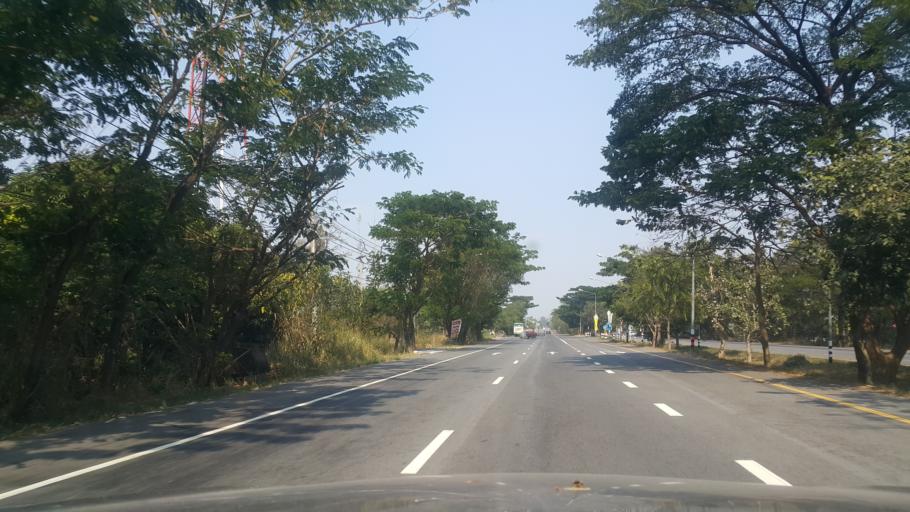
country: TH
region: Nakhon Ratchasima
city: Wang Nam Khiao
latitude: 14.5108
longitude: 101.9555
